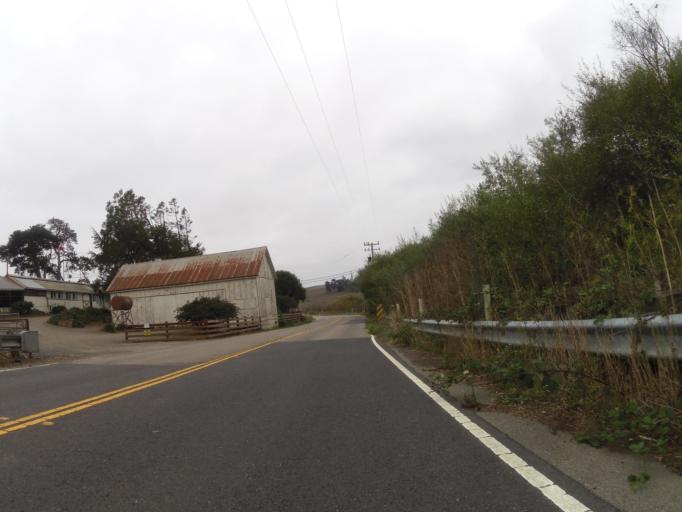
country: US
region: California
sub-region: Sonoma County
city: Occidental
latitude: 38.2732
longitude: -122.9006
